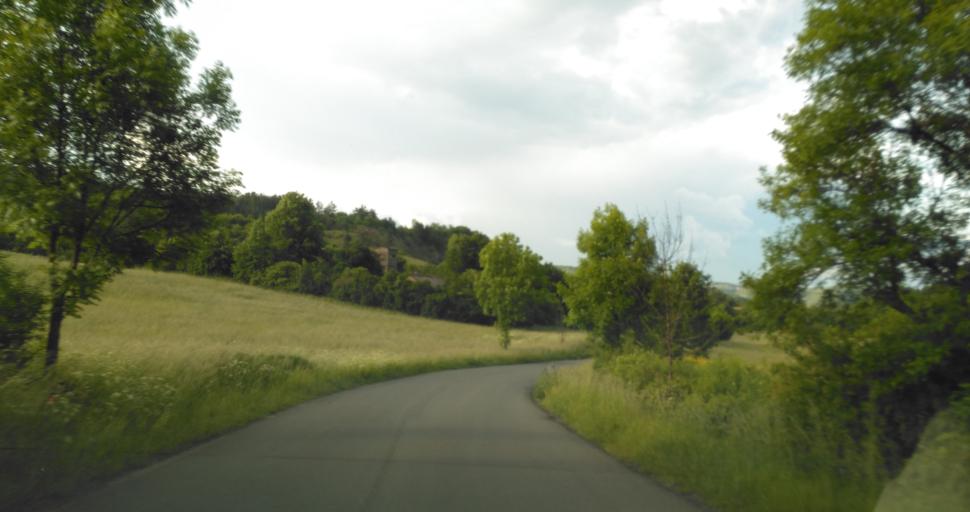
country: CZ
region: Central Bohemia
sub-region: Okres Beroun
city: Beroun
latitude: 49.9400
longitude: 14.0878
